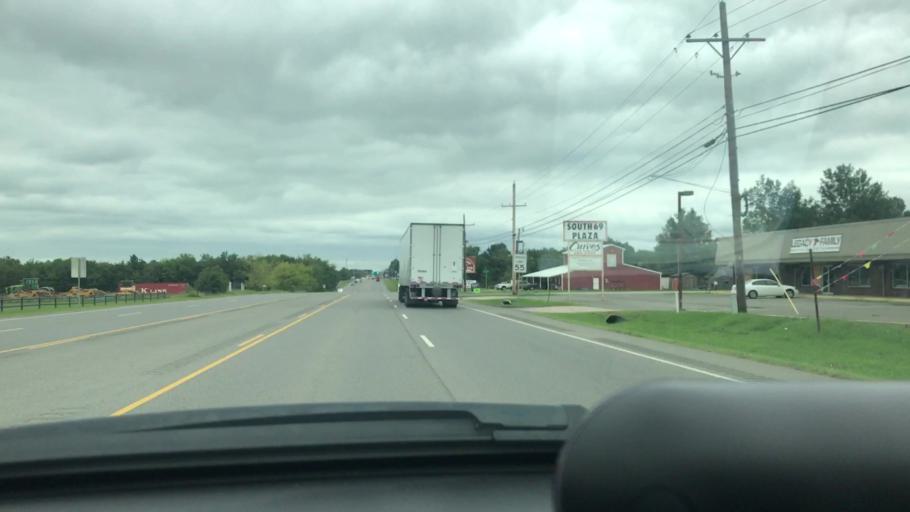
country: US
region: Oklahoma
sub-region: Wagoner County
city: Wagoner
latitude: 35.9373
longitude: -95.3952
